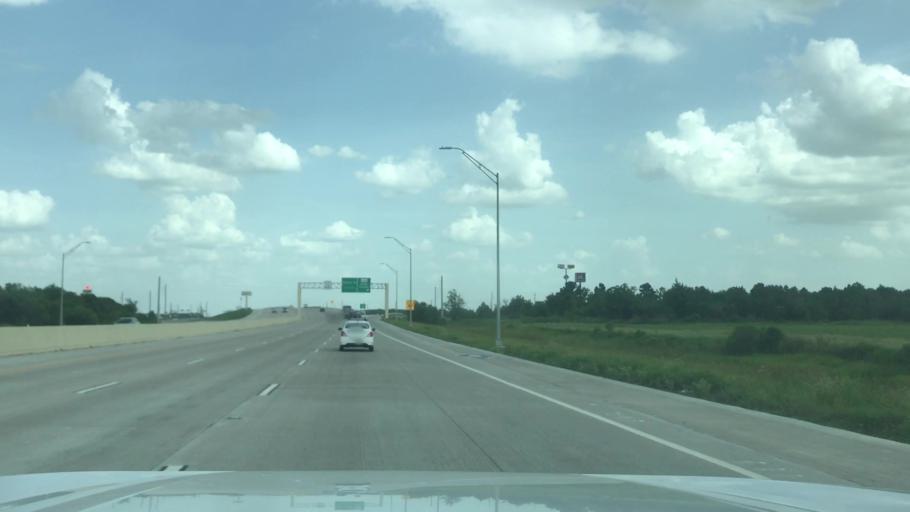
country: US
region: Texas
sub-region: Waller County
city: Waller
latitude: 30.0657
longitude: -95.9149
